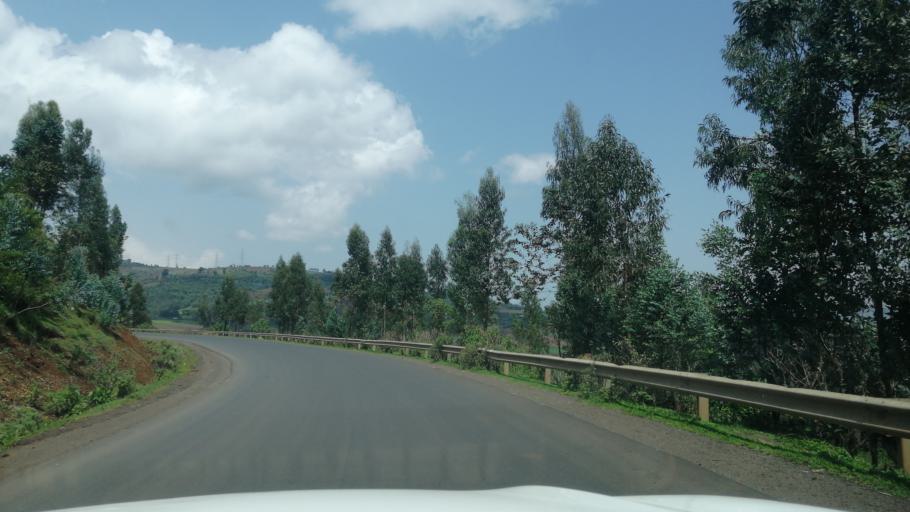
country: ET
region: Oromiya
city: Gedo
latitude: 8.9761
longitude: 37.5860
